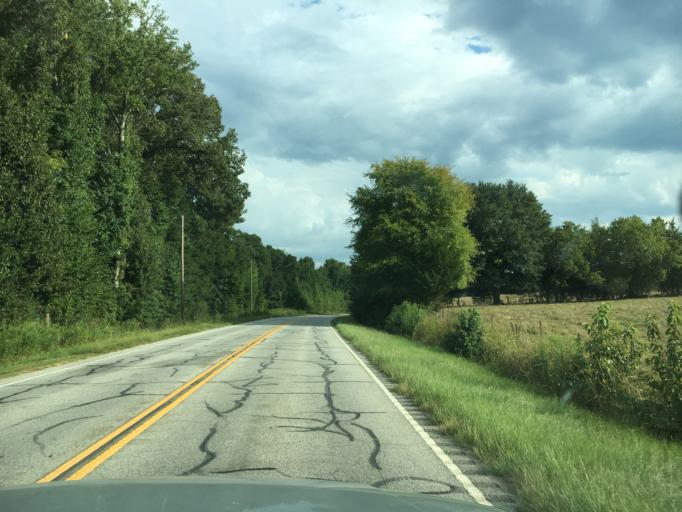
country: US
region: South Carolina
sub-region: Greenwood County
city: Ninety Six
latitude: 34.1992
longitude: -82.0297
